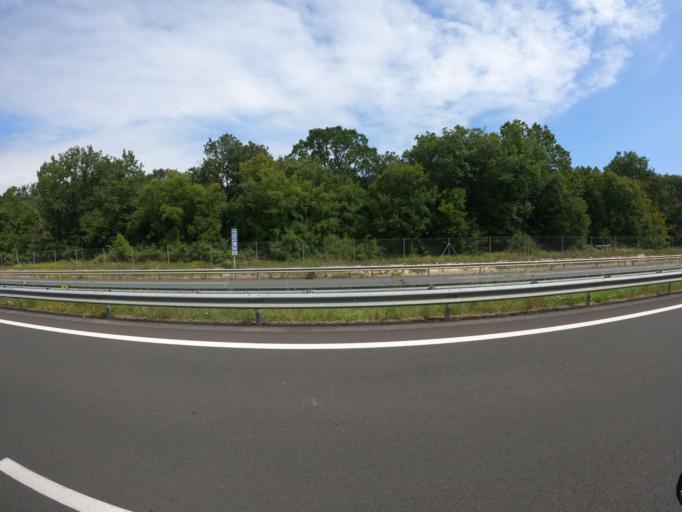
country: FR
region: Poitou-Charentes
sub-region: Departement de la Charente-Maritime
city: Courcon
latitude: 46.2200
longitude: -0.7994
